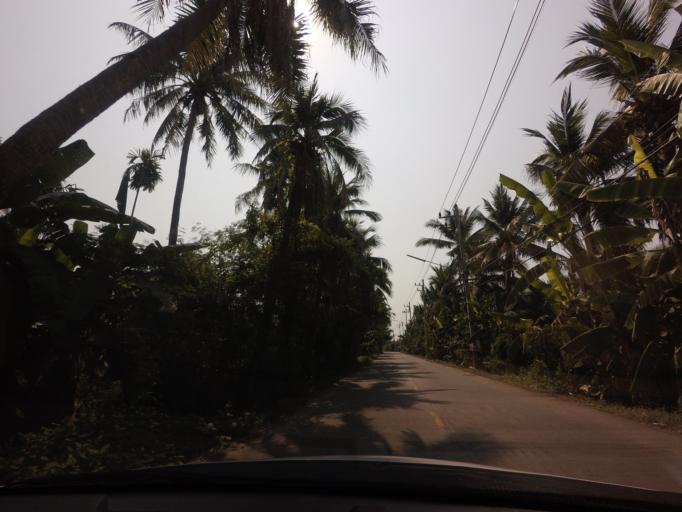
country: TH
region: Nakhon Pathom
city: Sam Phran
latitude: 13.7536
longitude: 100.2619
